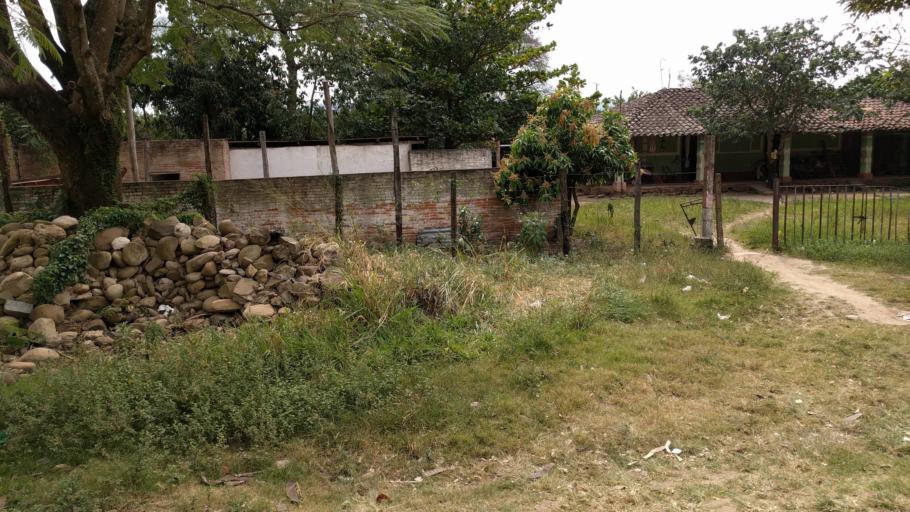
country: BO
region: Santa Cruz
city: Limoncito
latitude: -18.0394
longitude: -63.4112
